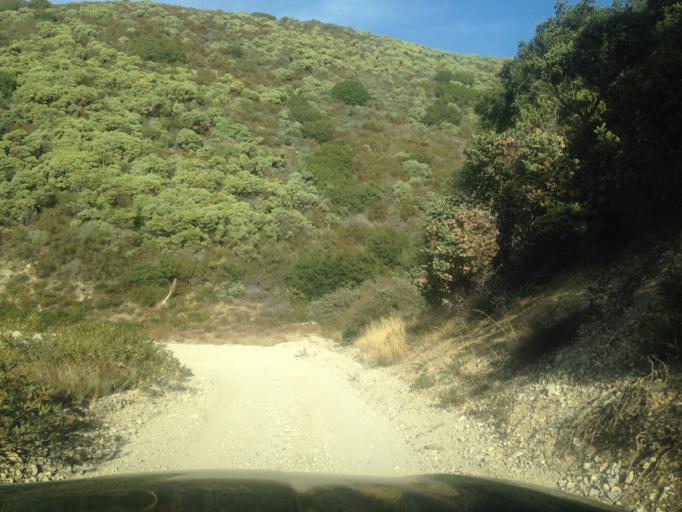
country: US
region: California
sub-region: San Bernardino County
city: Yucaipa
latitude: 34.1205
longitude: -117.0325
